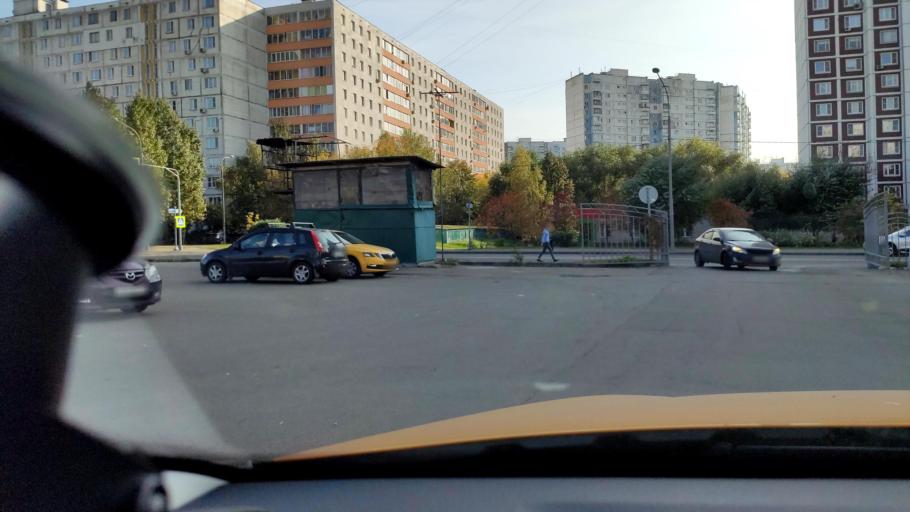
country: RU
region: Moscow
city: Altuf'yevskiy
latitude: 55.8875
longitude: 37.5901
